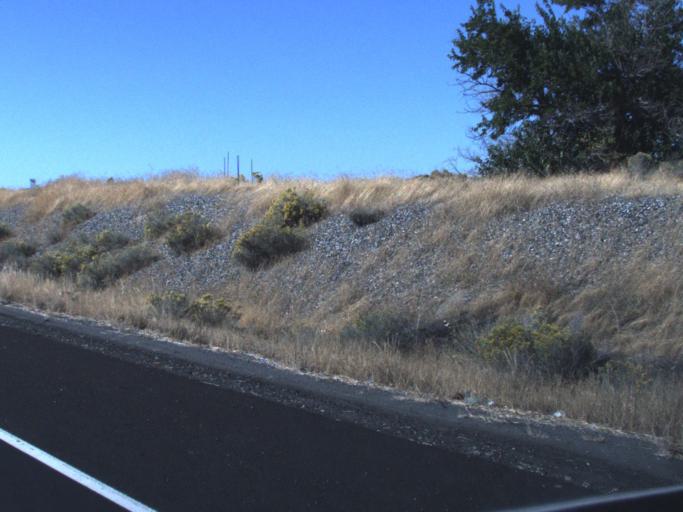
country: US
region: Washington
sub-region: Benton County
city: Richland
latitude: 46.3044
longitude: -119.2917
